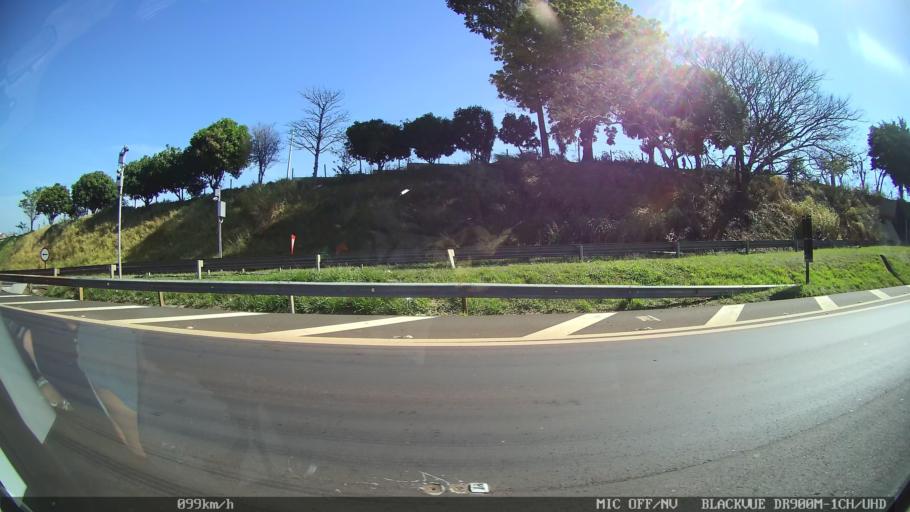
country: BR
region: Sao Paulo
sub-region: Franca
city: Franca
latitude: -20.5319
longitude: -47.4241
